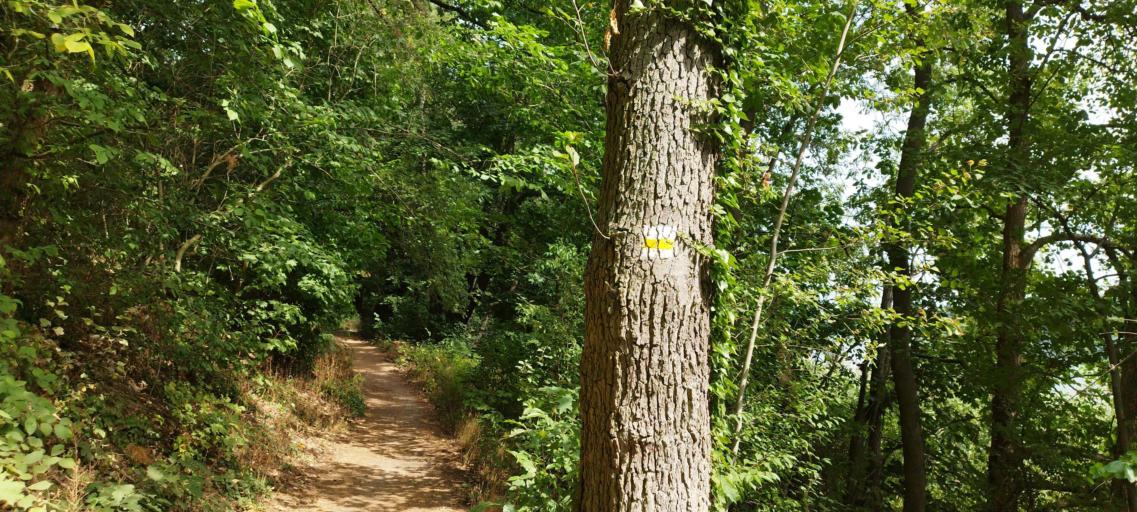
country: DE
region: Brandenburg
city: Strausberg
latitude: 52.5889
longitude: 13.8773
